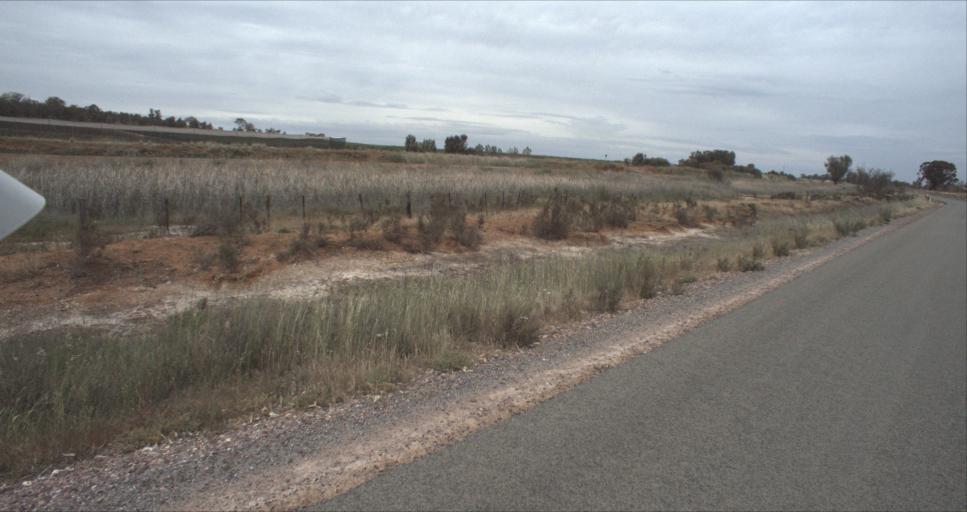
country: AU
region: New South Wales
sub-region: Leeton
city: Leeton
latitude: -34.4333
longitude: 146.3767
